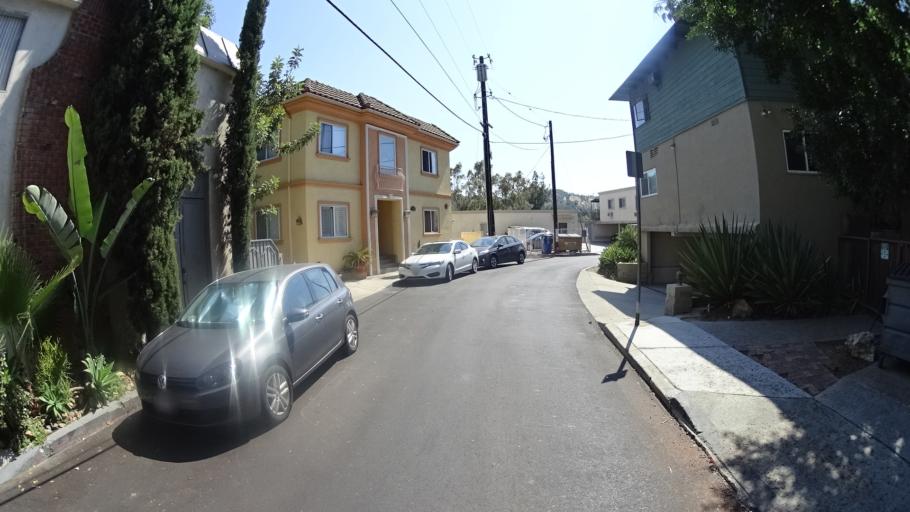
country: US
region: California
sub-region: Los Angeles County
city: North Hollywood
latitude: 34.1422
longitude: -118.3928
